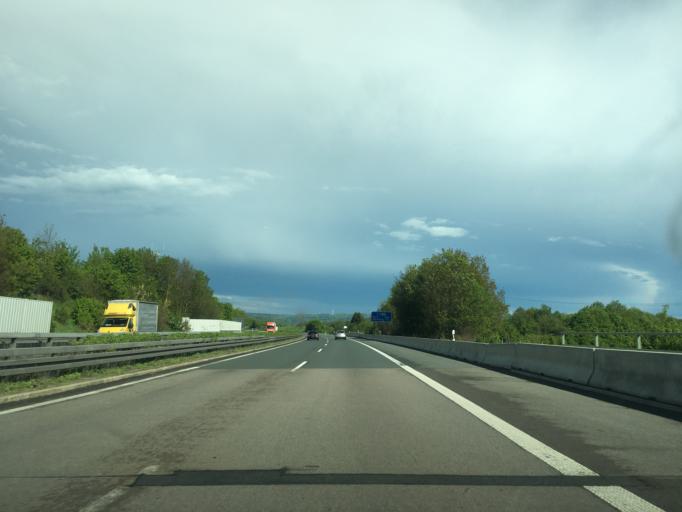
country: DE
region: Bavaria
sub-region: Regierungsbezirk Mittelfranken
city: Altdorf
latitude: 49.3785
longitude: 11.3503
